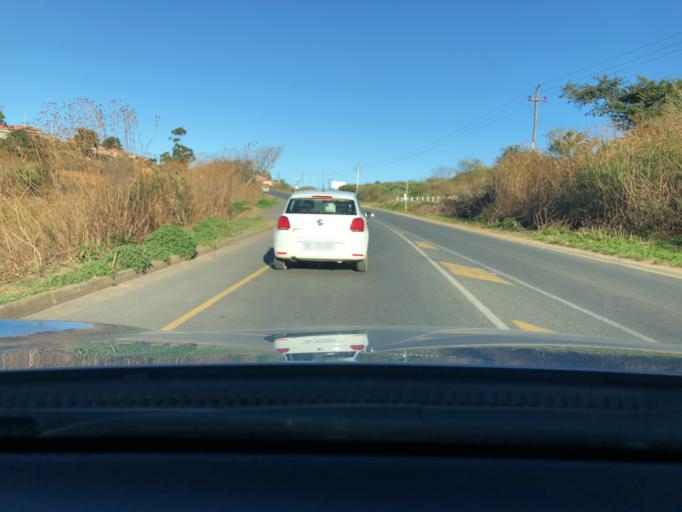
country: ZA
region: KwaZulu-Natal
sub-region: eThekwini Metropolitan Municipality
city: Umkomaas
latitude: -30.0343
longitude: 30.8349
